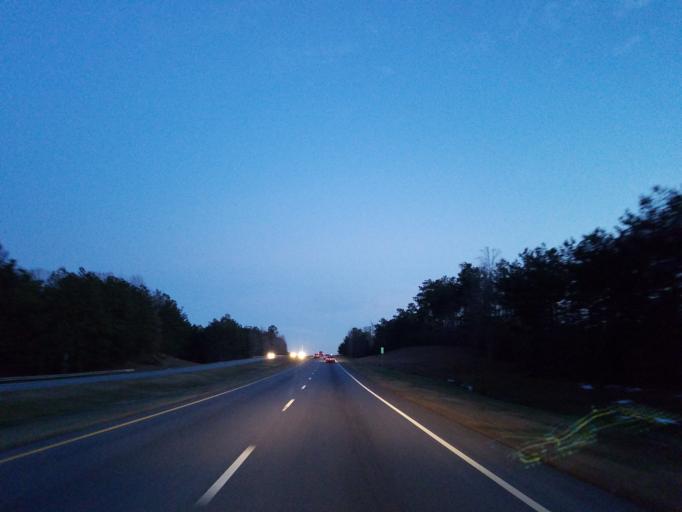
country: US
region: Georgia
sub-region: Paulding County
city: Dallas
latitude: 33.9061
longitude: -84.8167
